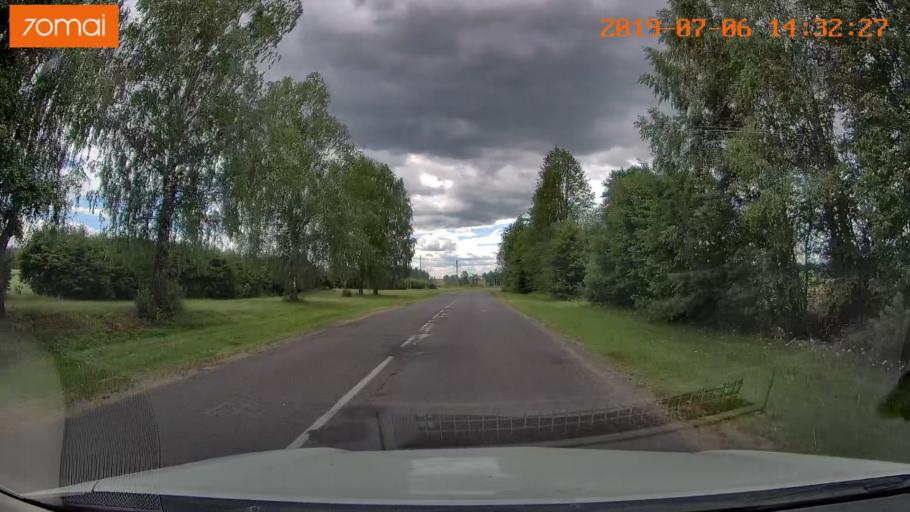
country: BY
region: Minsk
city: Ivyanyets
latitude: 53.9066
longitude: 26.7622
